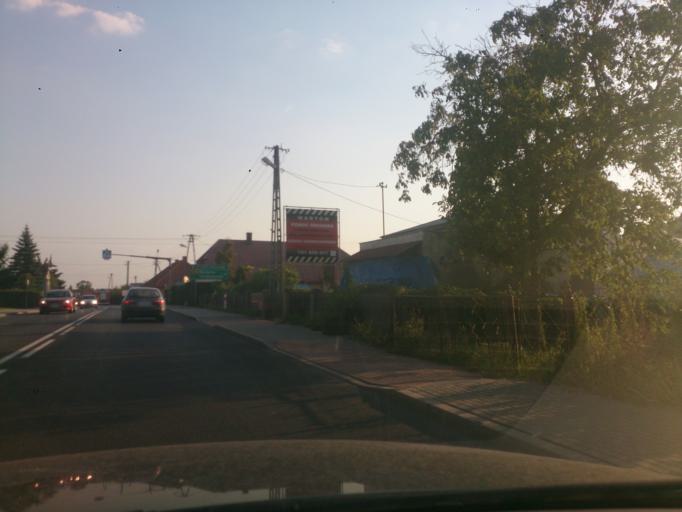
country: PL
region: Subcarpathian Voivodeship
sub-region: Powiat kolbuszowski
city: Majdan Krolewski
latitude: 50.3799
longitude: 21.7463
